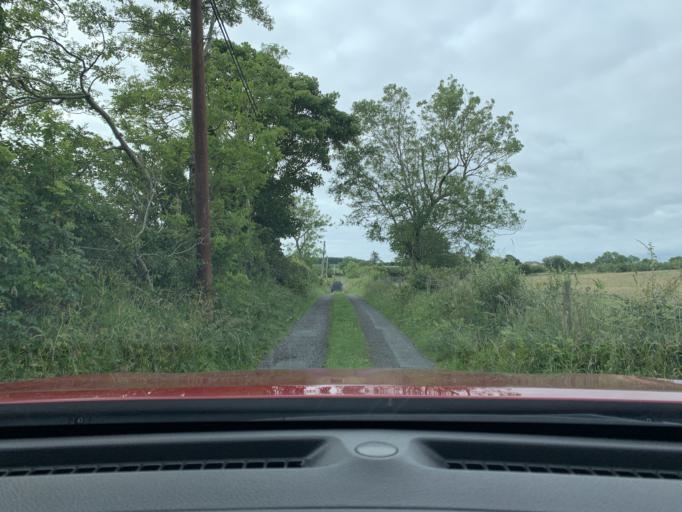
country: IE
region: Connaught
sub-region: Sligo
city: Sligo
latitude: 54.3801
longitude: -8.5215
